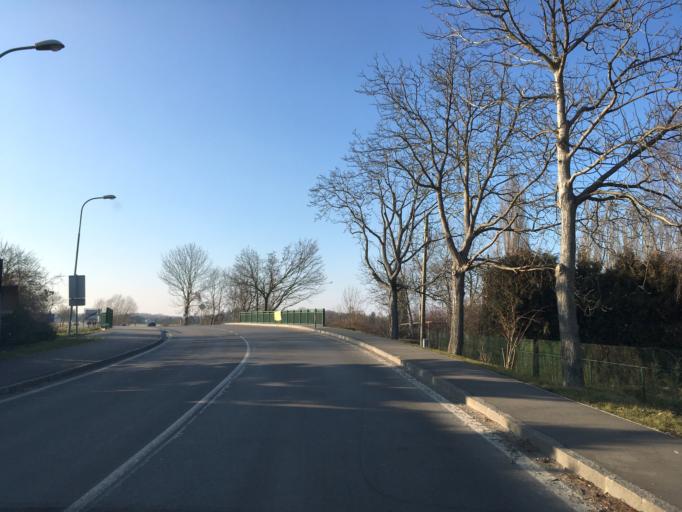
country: AT
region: Lower Austria
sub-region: Politischer Bezirk Tulln
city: Konigstetten
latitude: 48.3292
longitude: 16.1720
